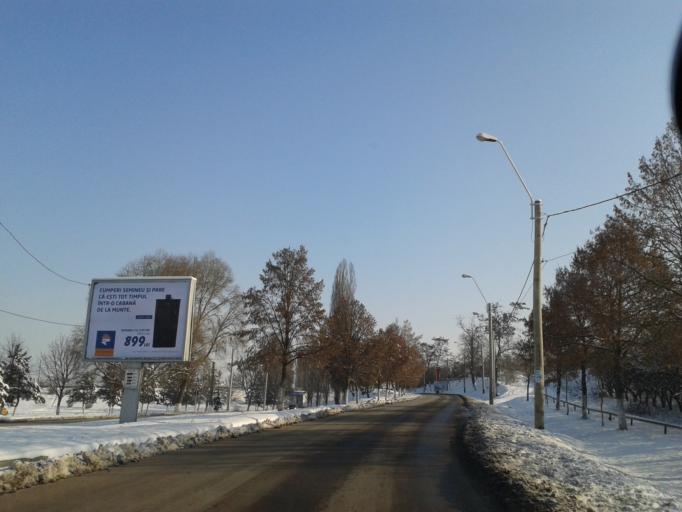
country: RO
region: Hunedoara
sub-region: Municipiul Deva
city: Deva
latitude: 45.8598
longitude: 22.9245
